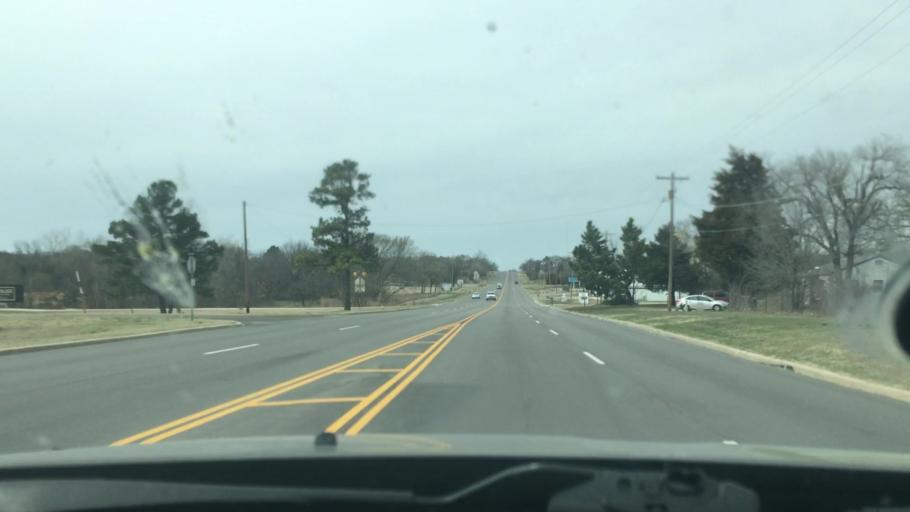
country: US
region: Oklahoma
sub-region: Seminole County
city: Seminole
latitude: 35.2500
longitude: -96.7036
